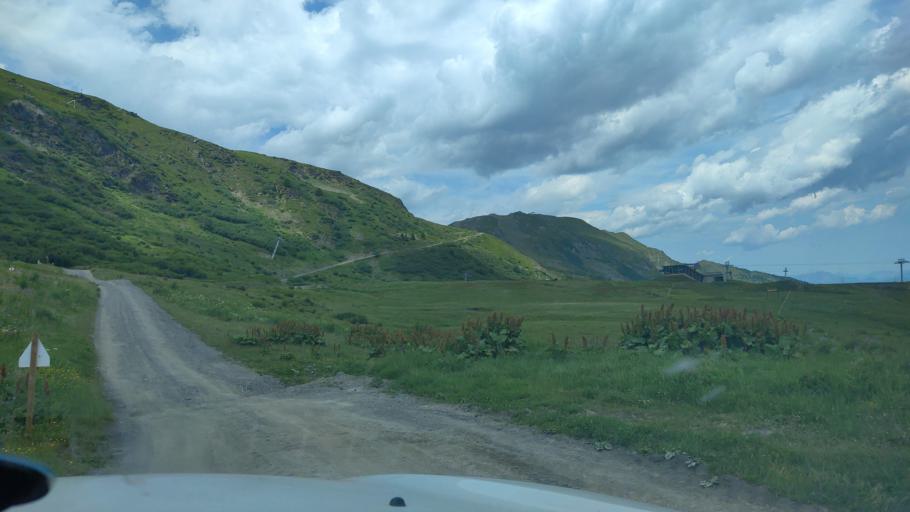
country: FR
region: Rhone-Alpes
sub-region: Departement de la Savoie
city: Meribel
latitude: 45.3769
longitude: 6.5575
